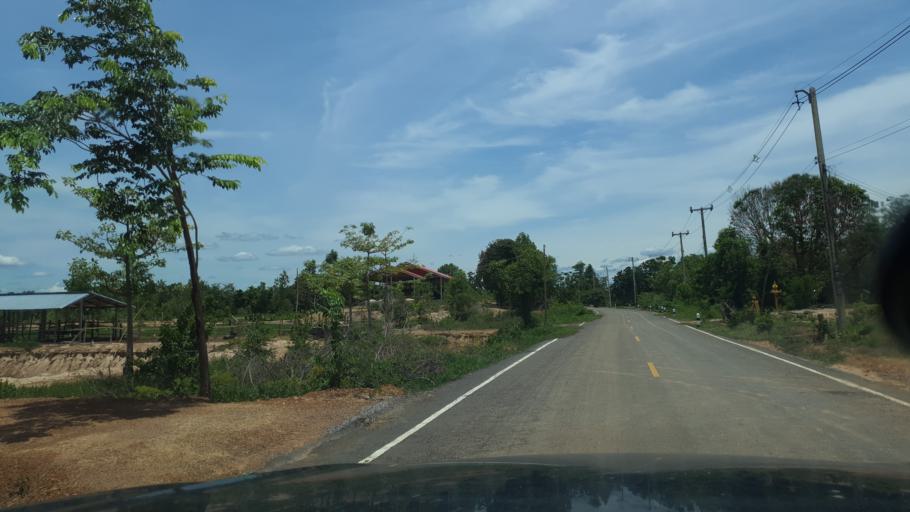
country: TH
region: Sukhothai
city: Ban Na
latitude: 17.1509
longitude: 99.6679
